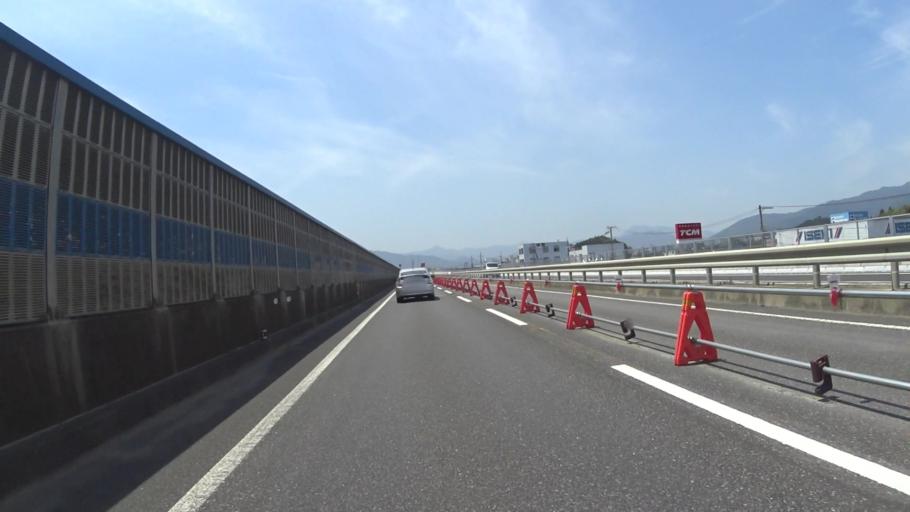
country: JP
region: Kyoto
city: Fukuchiyama
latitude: 35.2891
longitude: 135.1483
